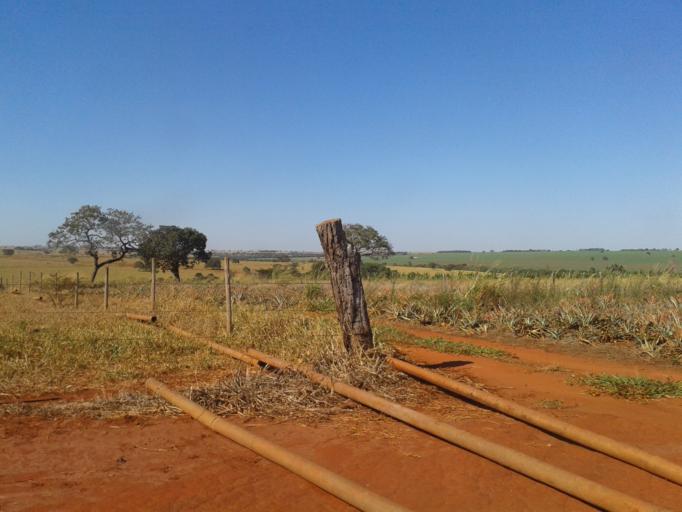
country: BR
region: Minas Gerais
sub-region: Centralina
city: Centralina
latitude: -18.7603
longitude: -49.2029
